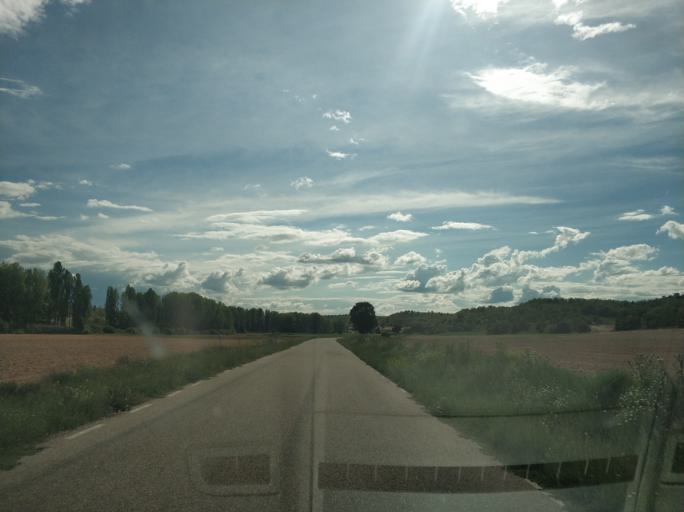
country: ES
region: Castille and Leon
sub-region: Provincia de Burgos
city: Brazacorta
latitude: 41.6907
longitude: -3.4097
